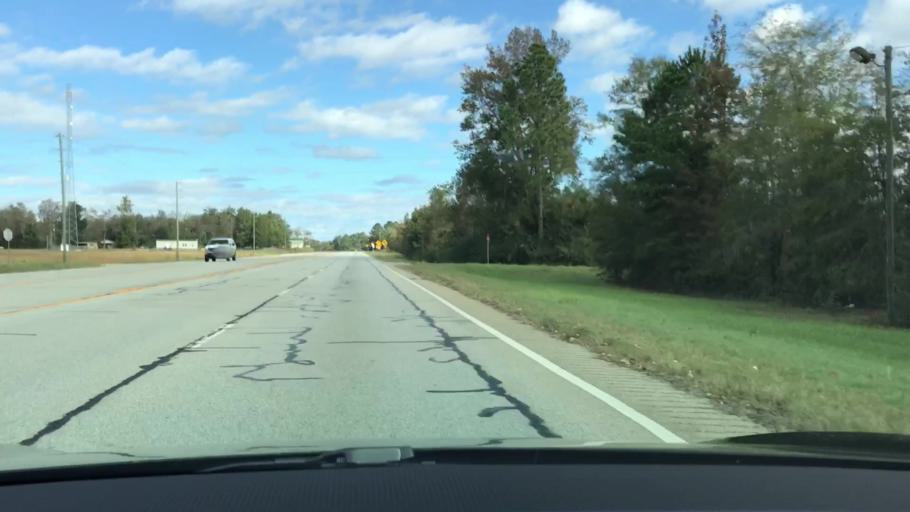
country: US
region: Georgia
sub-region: Jefferson County
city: Wadley
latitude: 32.8783
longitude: -82.3959
